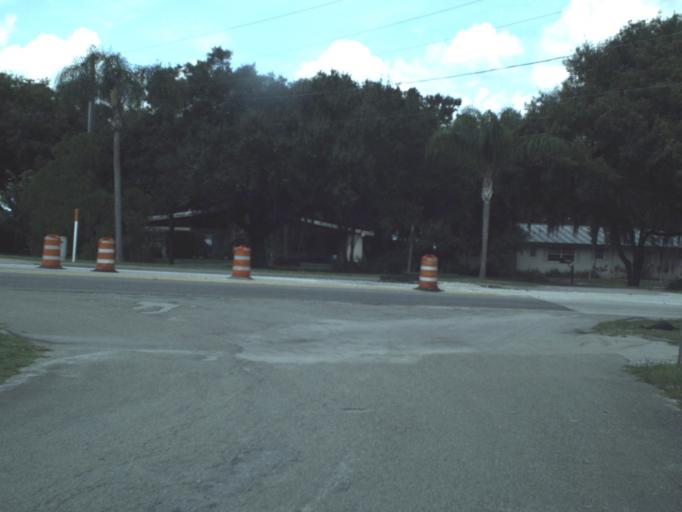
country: US
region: Florida
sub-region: Highlands County
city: Sebring
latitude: 27.4770
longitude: -81.4418
